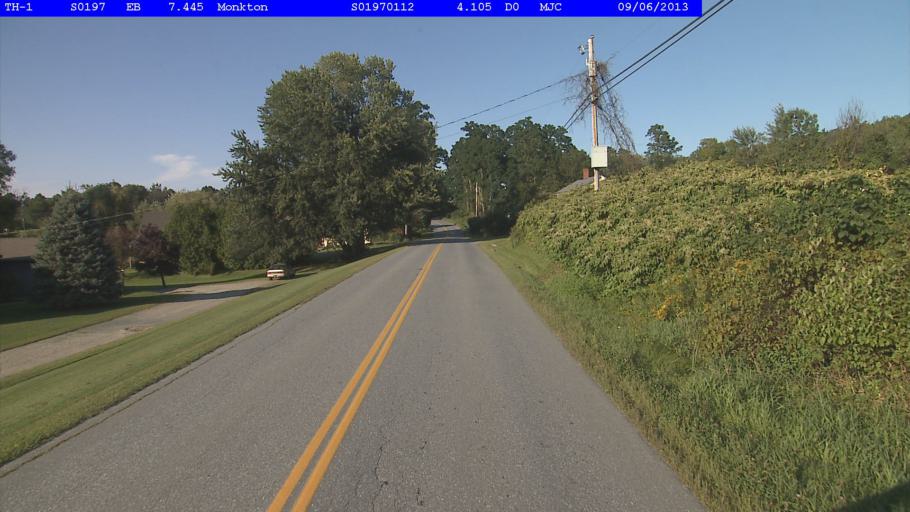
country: US
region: Vermont
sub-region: Chittenden County
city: Hinesburg
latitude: 44.2344
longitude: -73.1469
